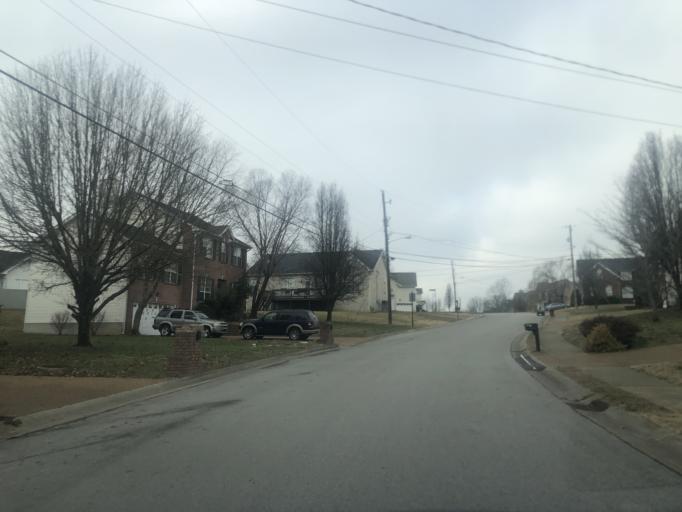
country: US
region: Tennessee
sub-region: Rutherford County
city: La Vergne
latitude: 36.0674
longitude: -86.6487
